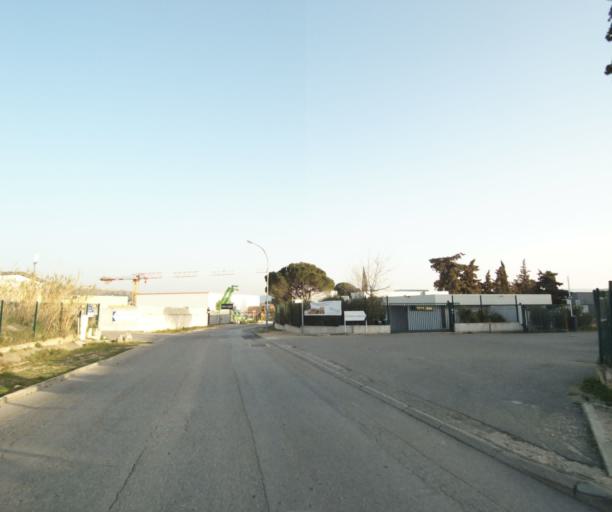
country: FR
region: Provence-Alpes-Cote d'Azur
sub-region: Departement des Bouches-du-Rhone
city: Vitrolles
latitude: 43.4366
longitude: 5.2501
